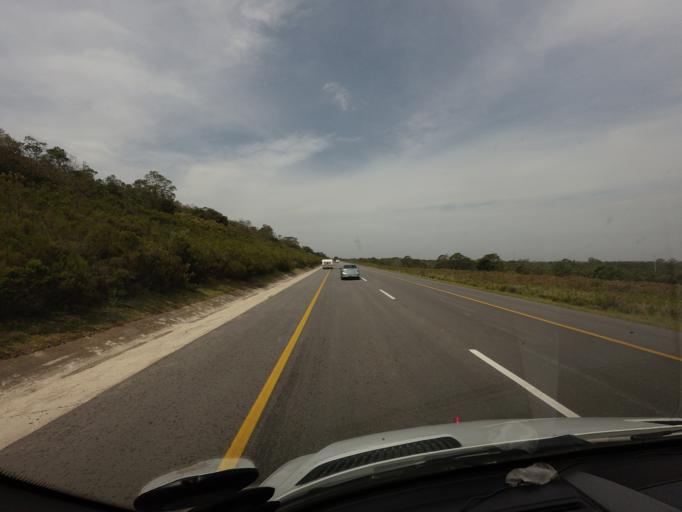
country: ZA
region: Eastern Cape
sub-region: Cacadu District Municipality
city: Kruisfontein
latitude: -33.9947
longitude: 24.7232
